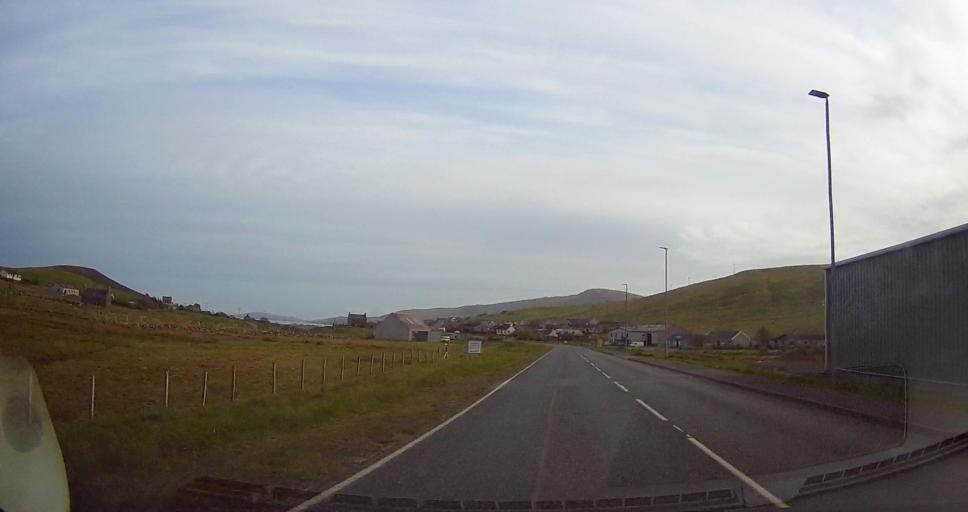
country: GB
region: Scotland
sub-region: Shetland Islands
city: Sandwick
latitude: 60.0577
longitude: -1.2241
